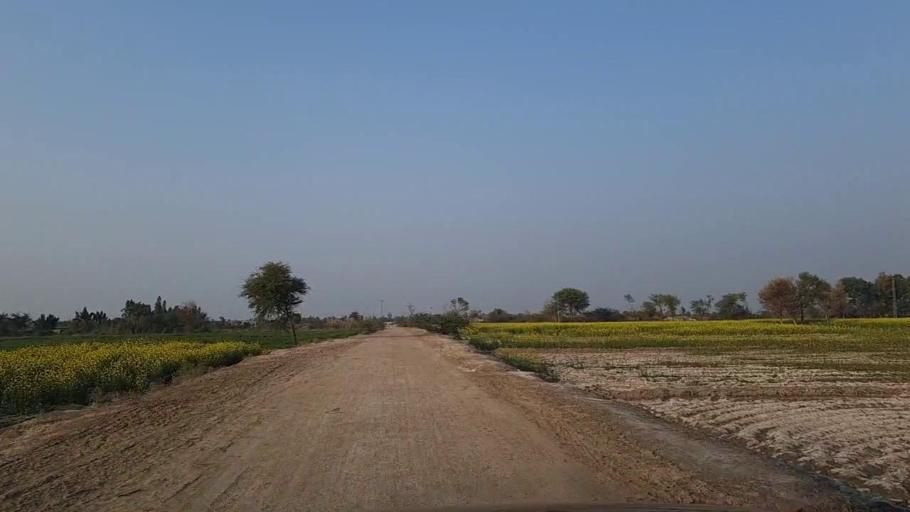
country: PK
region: Sindh
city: Daur
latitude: 26.4078
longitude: 68.3829
